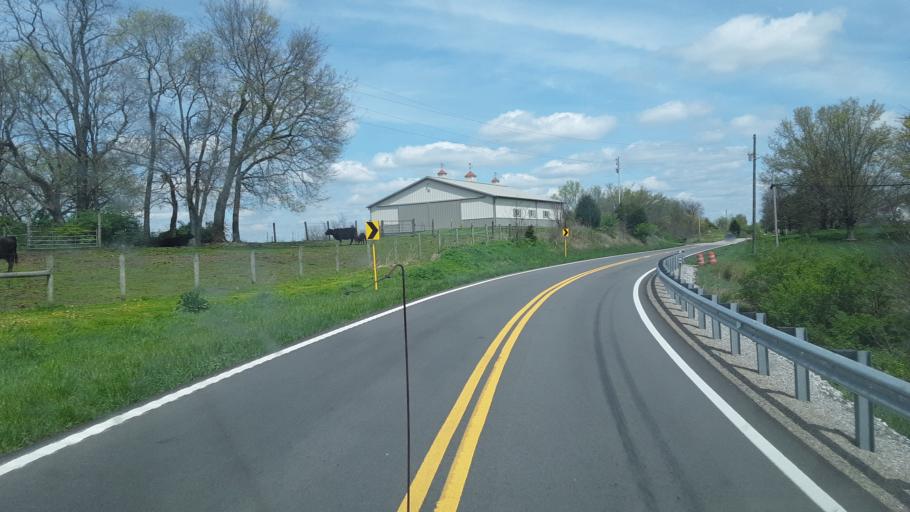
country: US
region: Kentucky
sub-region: Grant County
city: Dry Ridge
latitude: 38.6715
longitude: -84.6376
